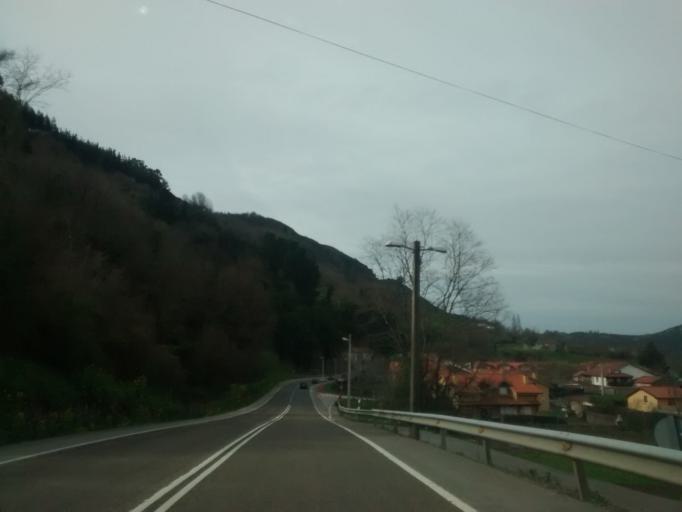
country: ES
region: Cantabria
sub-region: Provincia de Cantabria
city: Corvera
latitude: 43.2523
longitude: -3.9477
